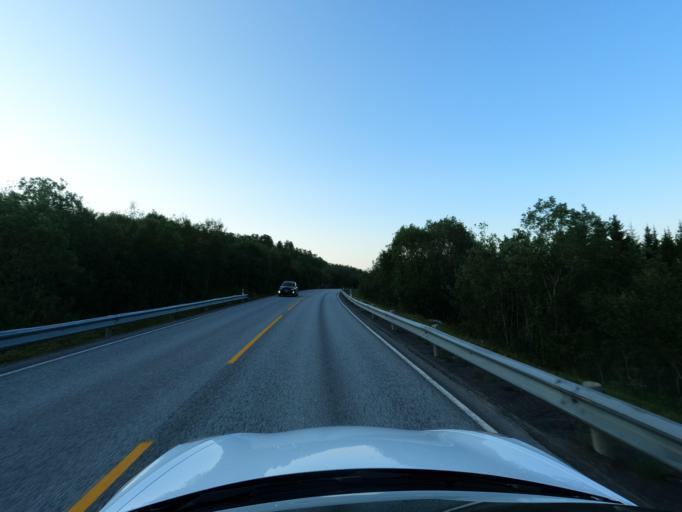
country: NO
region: Troms
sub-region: Harstad
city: Harstad
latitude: 68.7365
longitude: 16.5538
